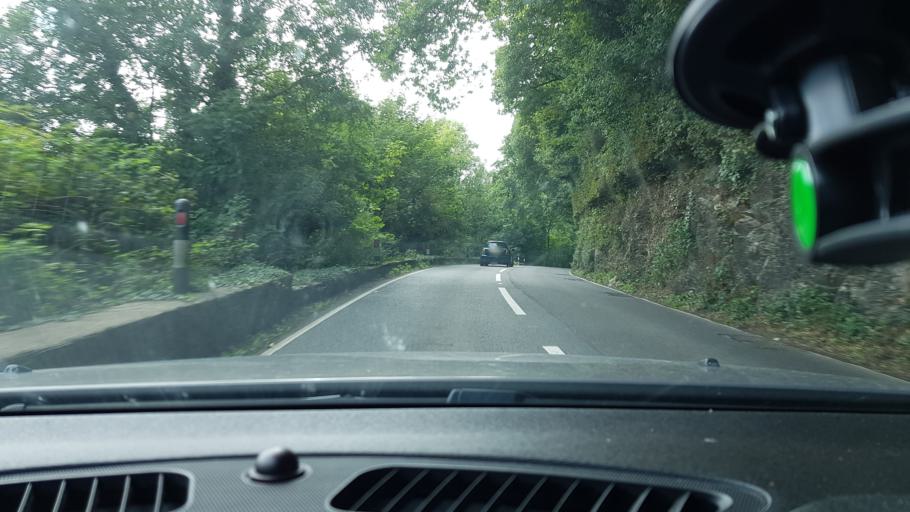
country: GB
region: England
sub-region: Cornwall
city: Helland
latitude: 50.5715
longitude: -4.7438
